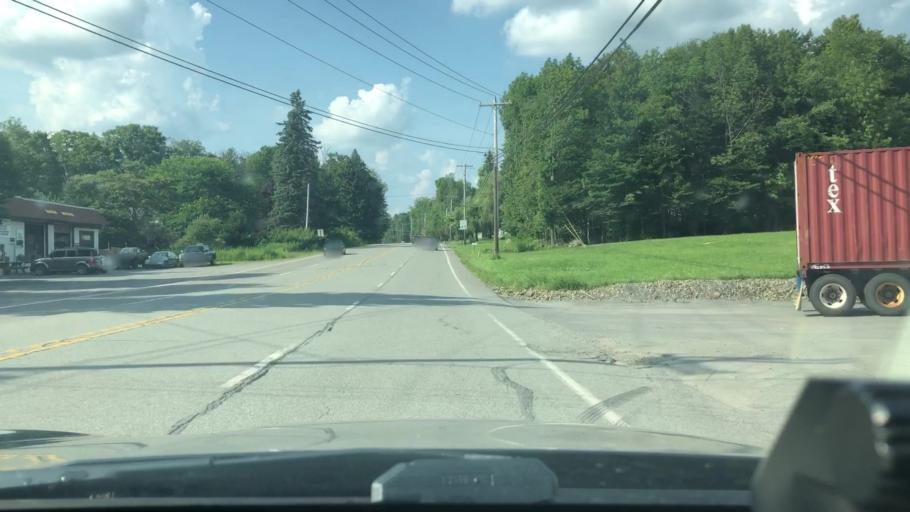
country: US
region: Pennsylvania
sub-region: Lackawanna County
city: Moscow
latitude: 41.2702
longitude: -75.5068
